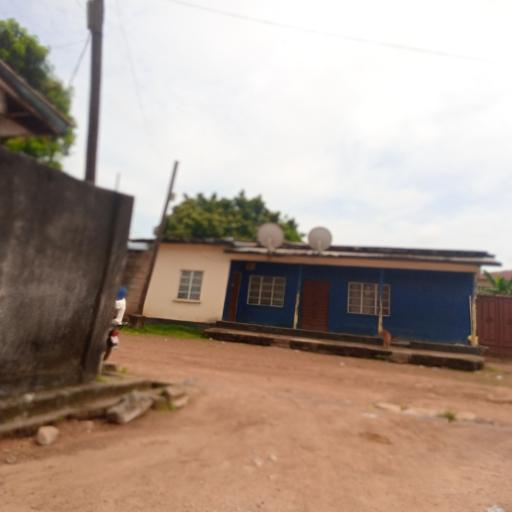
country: SL
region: Eastern Province
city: Kenema
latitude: 7.8868
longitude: -11.1893
